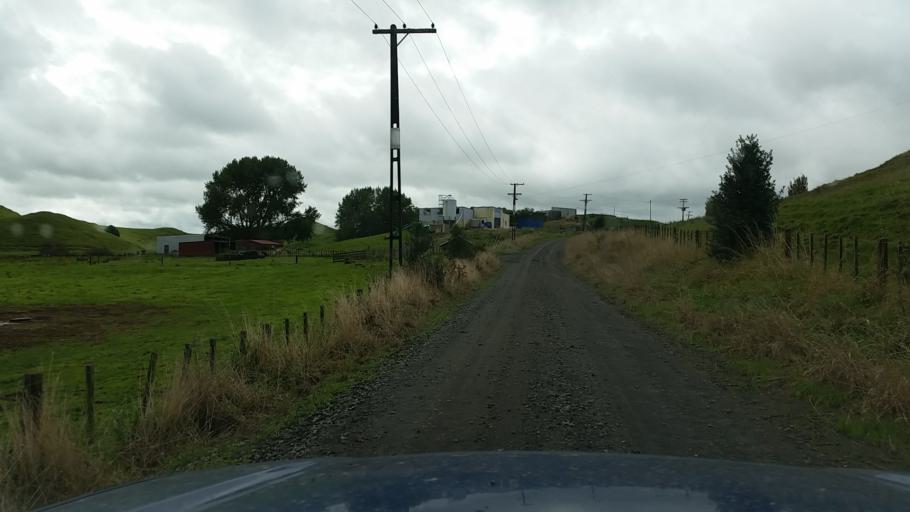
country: NZ
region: Taranaki
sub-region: South Taranaki District
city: Eltham
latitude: -39.3528
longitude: 174.4352
